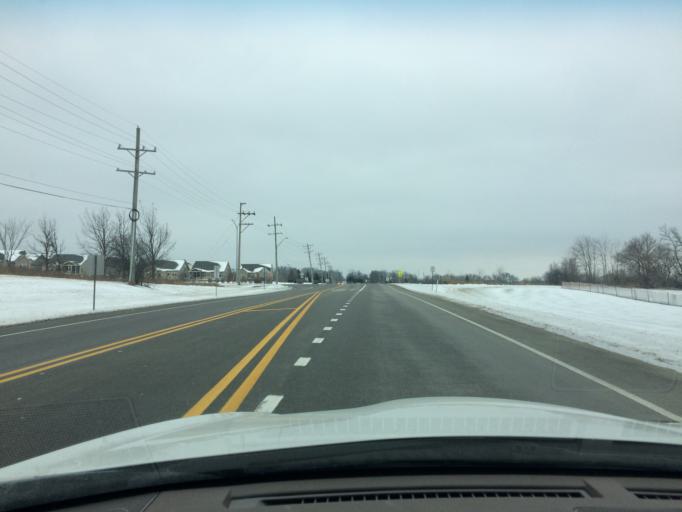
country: US
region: Illinois
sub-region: Kane County
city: Saint Charles
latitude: 41.8985
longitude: -88.3595
